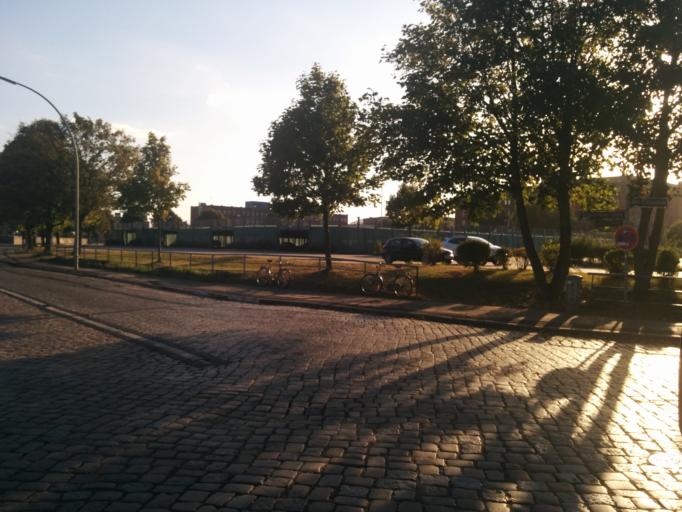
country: DE
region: Hamburg
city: St. Pauli
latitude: 53.5413
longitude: 9.9665
